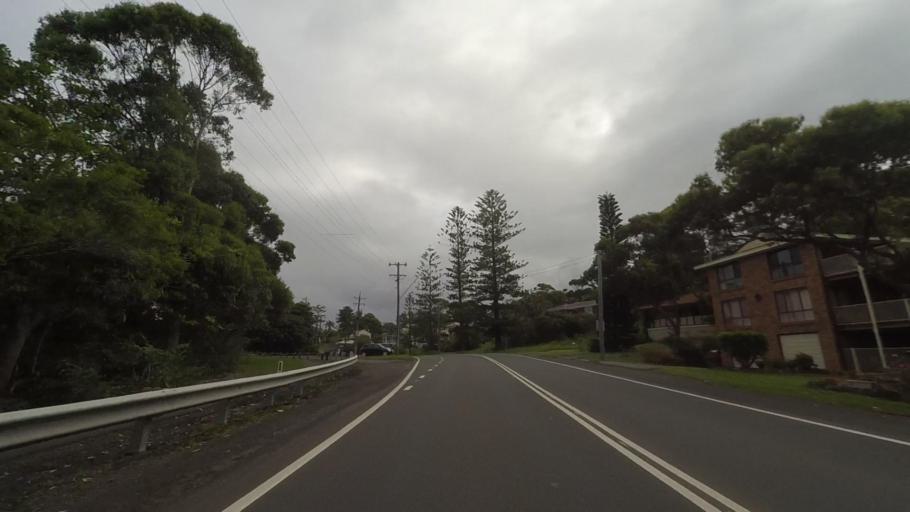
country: AU
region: New South Wales
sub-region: Wollongong
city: Bulli
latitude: -34.2963
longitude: 150.9413
